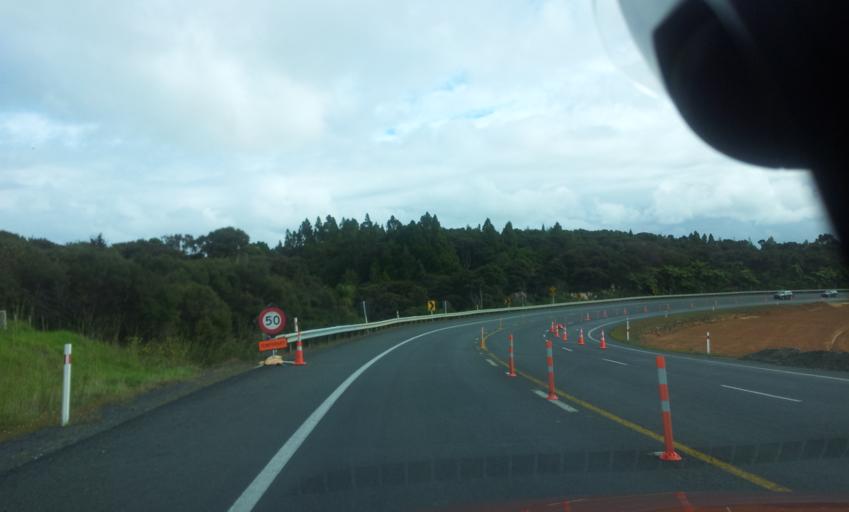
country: NZ
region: Northland
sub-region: Whangarei
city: Ruakaka
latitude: -36.0503
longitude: 174.4174
